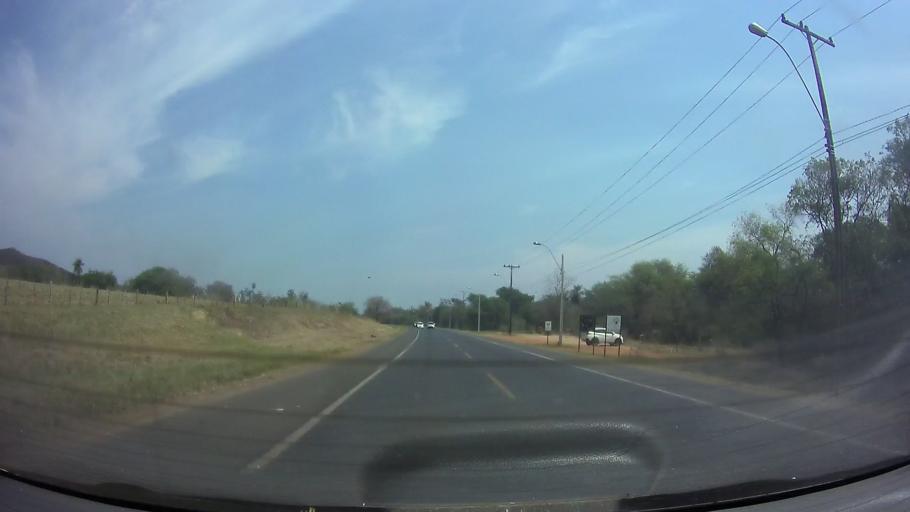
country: PY
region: Central
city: Itaugua
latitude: -25.3440
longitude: -57.3415
